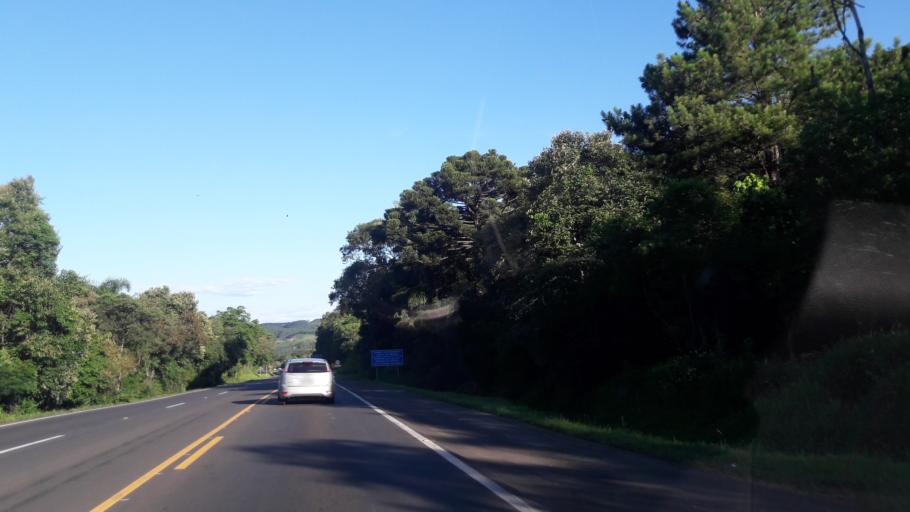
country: BR
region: Parana
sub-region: Prudentopolis
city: Prudentopolis
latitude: -25.3124
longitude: -51.1816
